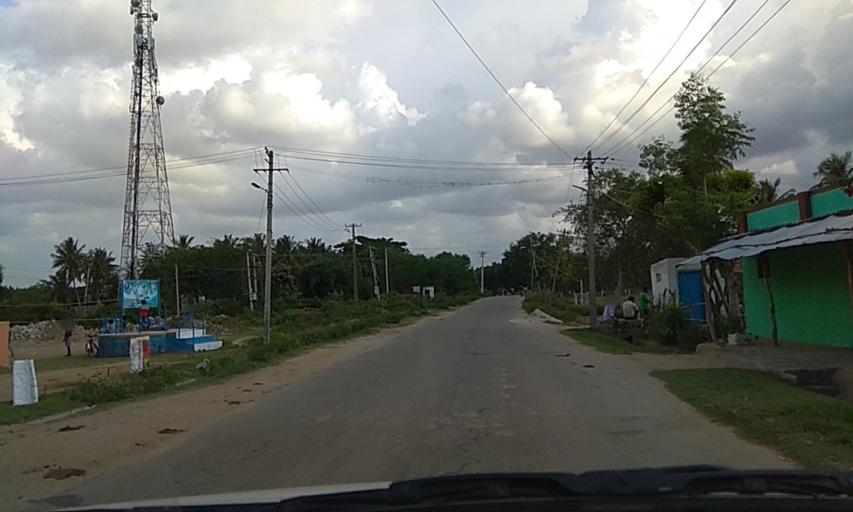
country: IN
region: Karnataka
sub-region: Chamrajnagar
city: Gundlupet
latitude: 11.8891
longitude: 76.7466
